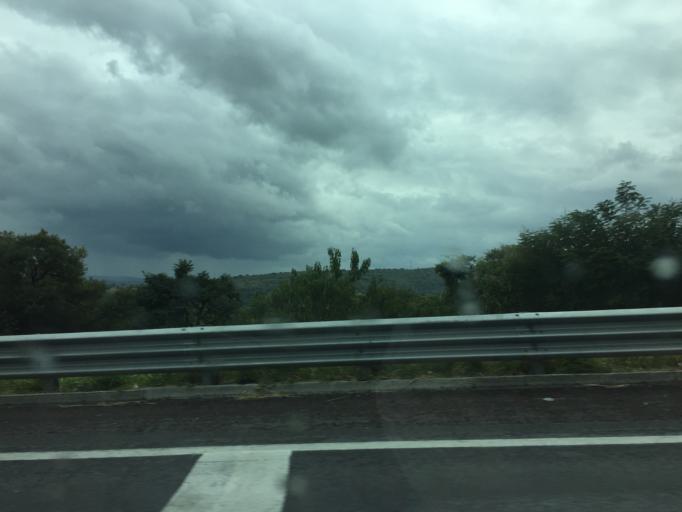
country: MX
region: Jalisco
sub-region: Tonala
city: Mismaloya (Fraccionamiento Pedregal de Santa Martha)
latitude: 20.6025
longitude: -103.1540
